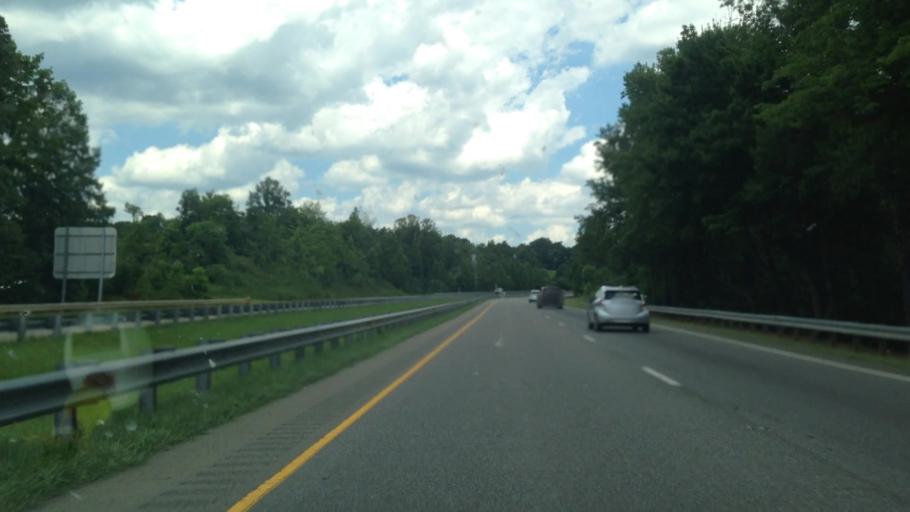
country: US
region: North Carolina
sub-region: Rockingham County
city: Stoneville
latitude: 36.4858
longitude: -79.9249
